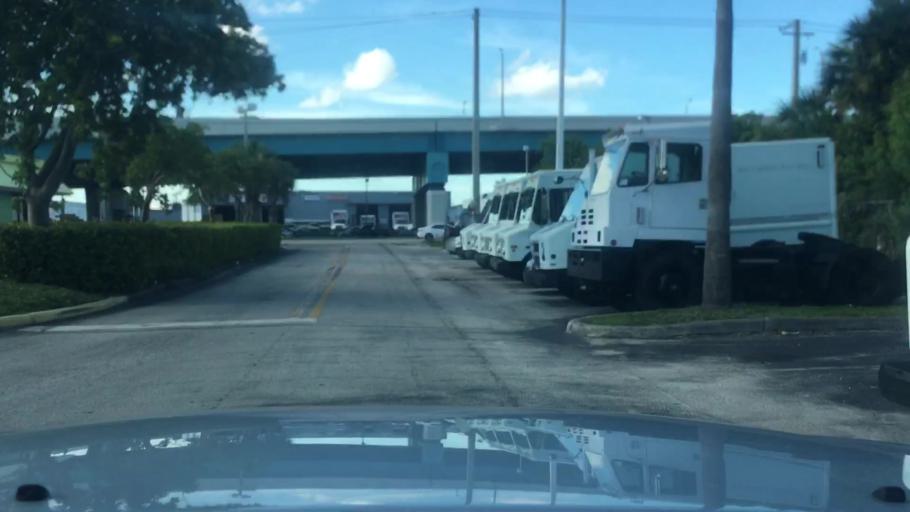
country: US
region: Florida
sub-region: Miami-Dade County
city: Virginia Gardens
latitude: 25.7963
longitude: -80.3179
